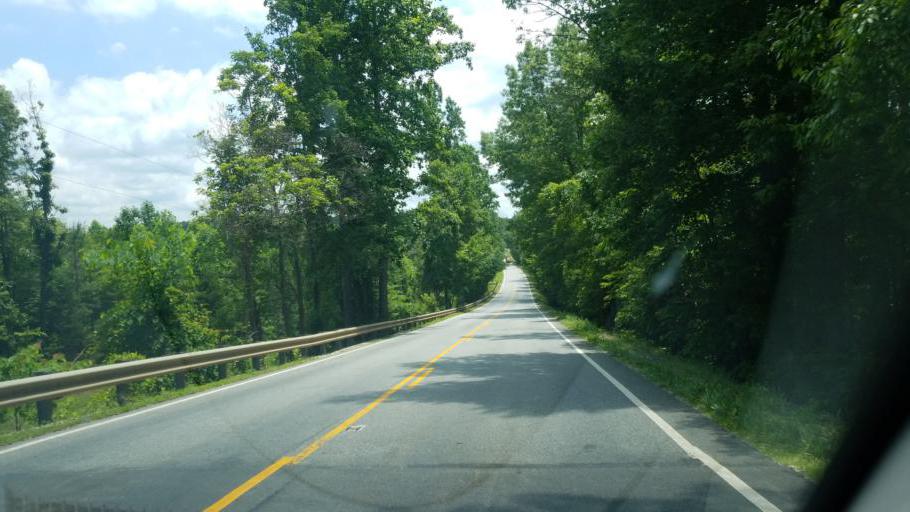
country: US
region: Virginia
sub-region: Nelson County
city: Lovingston
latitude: 37.5703
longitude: -78.8544
